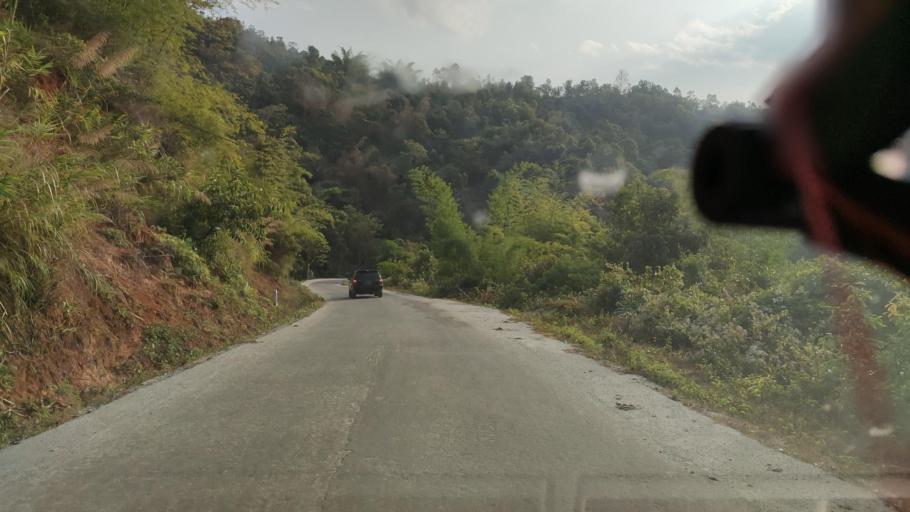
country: CN
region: Yunnan
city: Menghai
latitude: 21.4519
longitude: 99.6590
